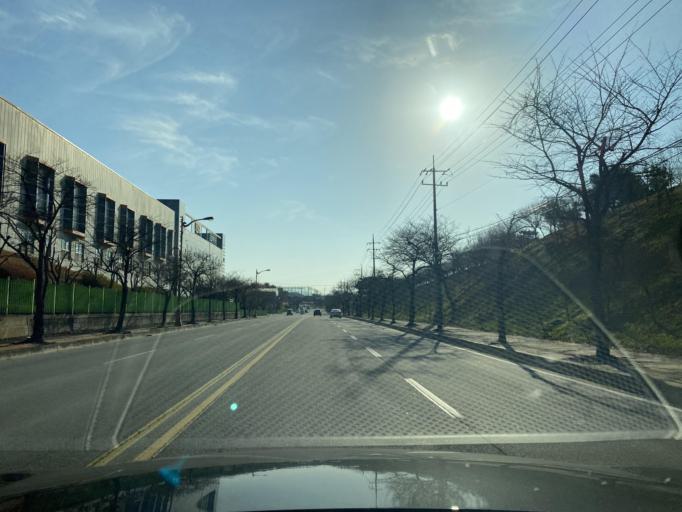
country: KR
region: Chungcheongnam-do
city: Yesan
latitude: 36.7163
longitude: 126.8434
